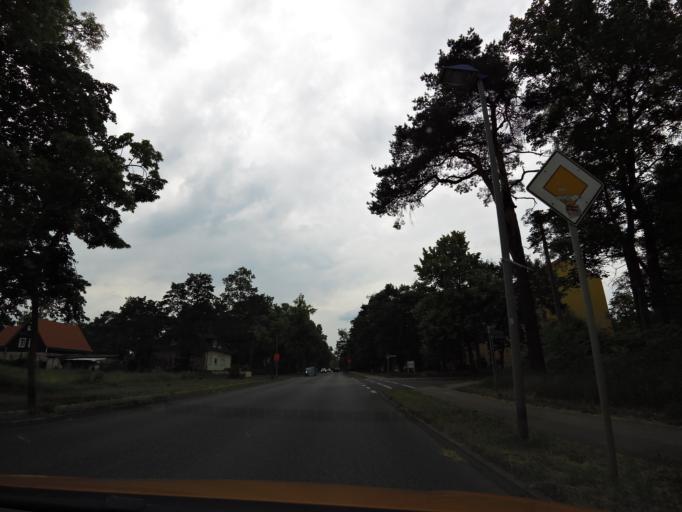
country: DE
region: Brandenburg
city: Zossen
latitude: 52.1648
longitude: 13.4735
